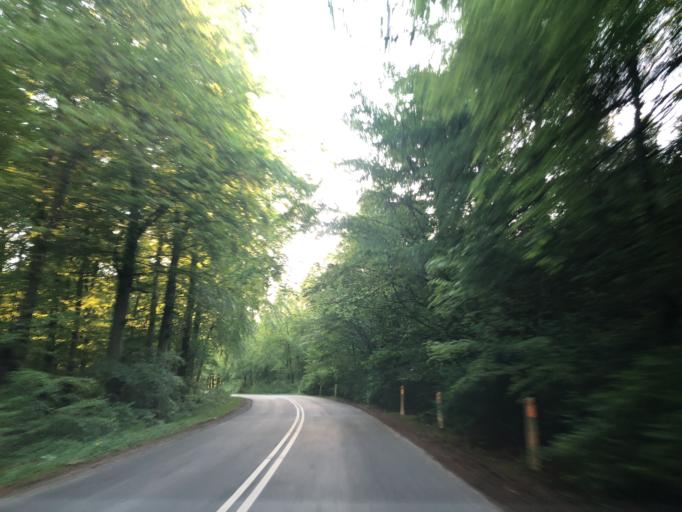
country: DK
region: Zealand
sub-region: Koge Kommune
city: Bjaeverskov
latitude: 55.4265
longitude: 12.0757
